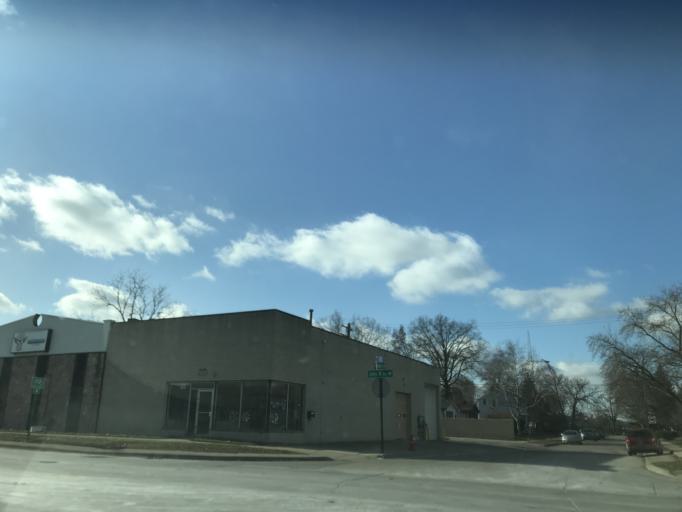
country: US
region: Michigan
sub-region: Oakland County
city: Madison Heights
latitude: 42.4784
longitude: -83.1046
